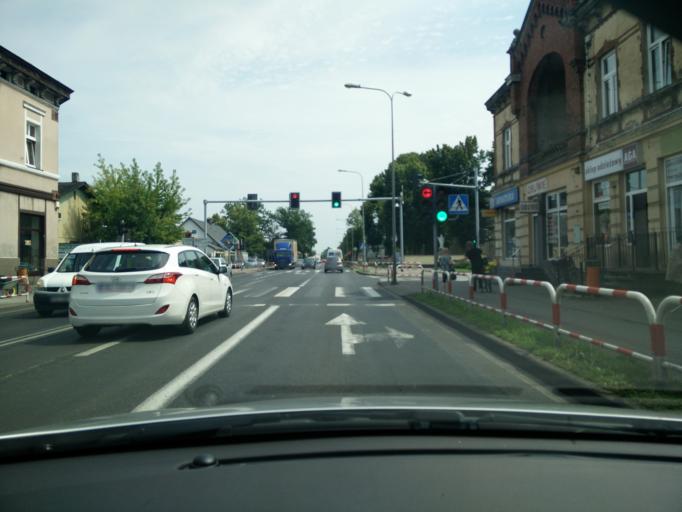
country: PL
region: Greater Poland Voivodeship
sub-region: Powiat slupecki
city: Strzalkowo
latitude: 52.3101
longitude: 17.8178
